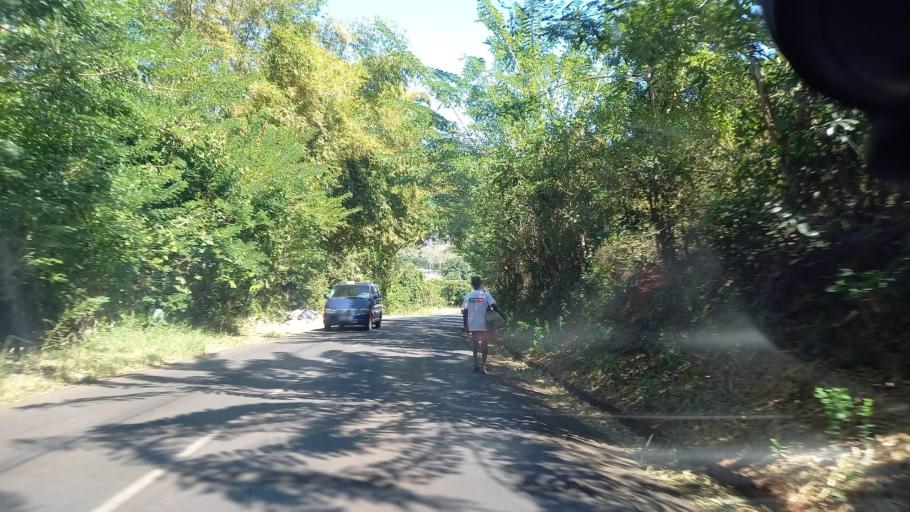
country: YT
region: Tsingoni
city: Tsingoni
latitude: -12.7844
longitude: 45.1443
